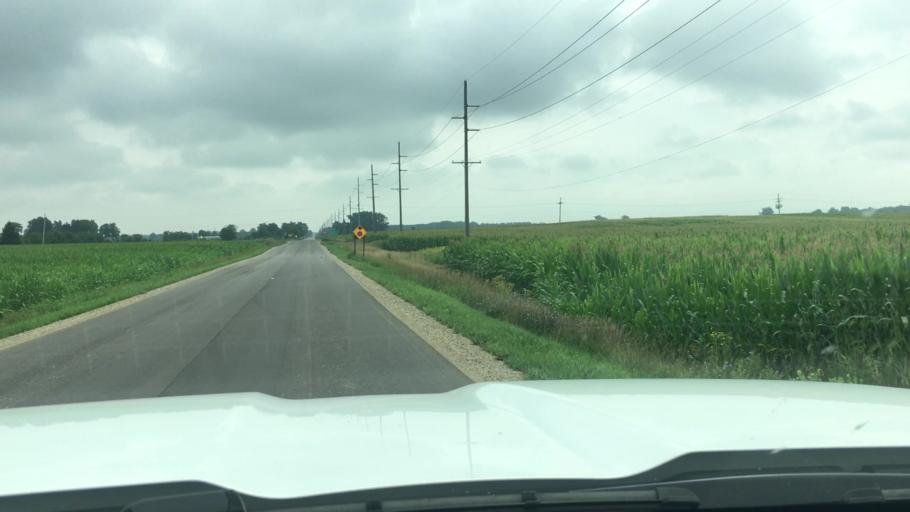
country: US
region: Michigan
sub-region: Sanilac County
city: Brown City
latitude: 43.2563
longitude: -82.9854
